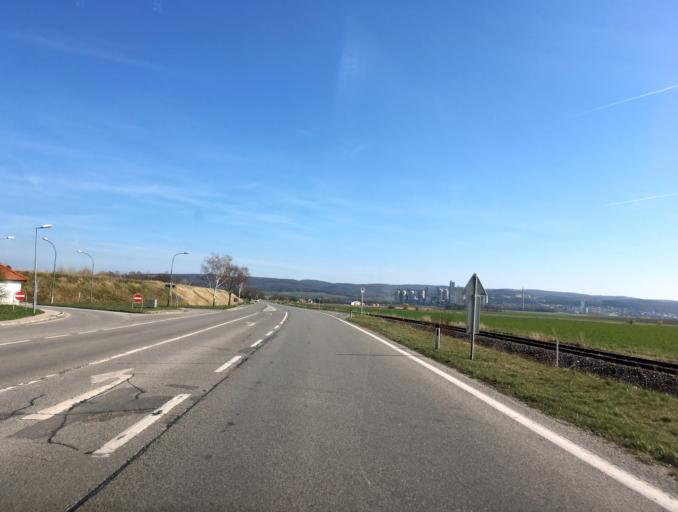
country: AT
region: Lower Austria
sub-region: Politischer Bezirk Bruck an der Leitha
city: Gotzendorf an der Leitha
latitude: 48.0052
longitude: 16.5896
